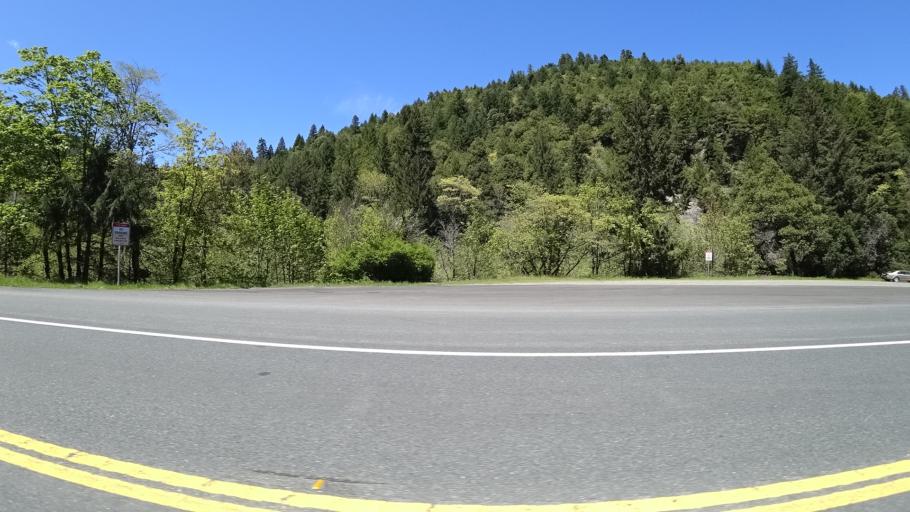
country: US
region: California
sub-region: Humboldt County
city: Willow Creek
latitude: 40.9211
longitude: -123.6971
